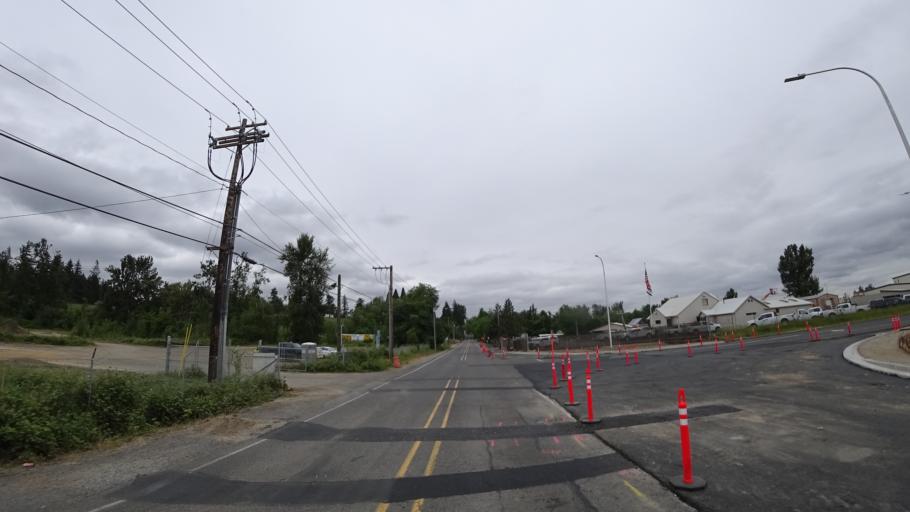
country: US
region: Oregon
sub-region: Multnomah County
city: Fairview
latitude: 45.5429
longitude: -122.4258
